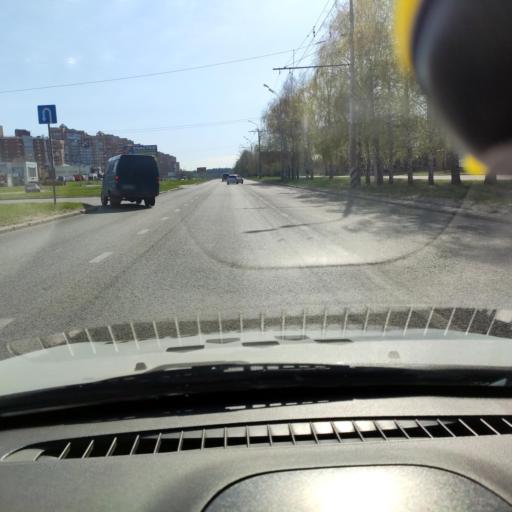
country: RU
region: Samara
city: Tol'yatti
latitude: 53.4996
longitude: 49.2706
